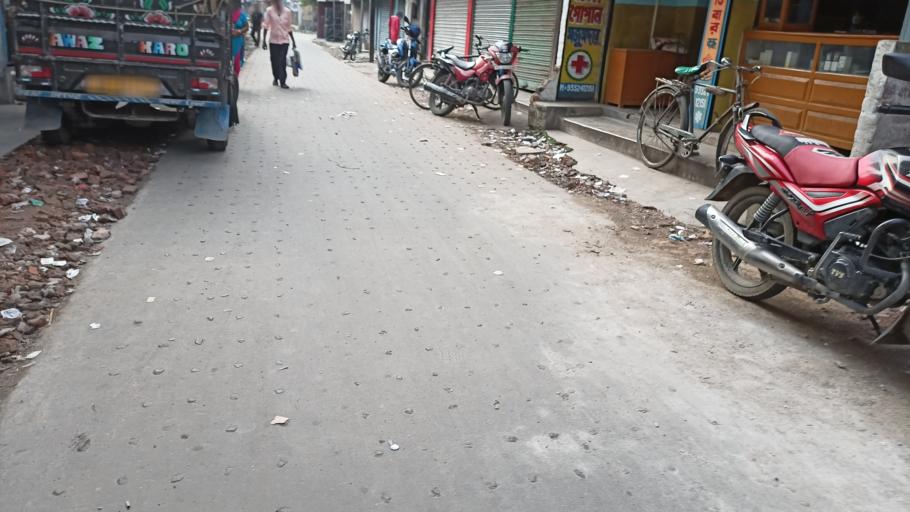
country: IN
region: West Bengal
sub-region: North 24 Parganas
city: Bangaon
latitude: 23.0458
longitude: 88.8303
